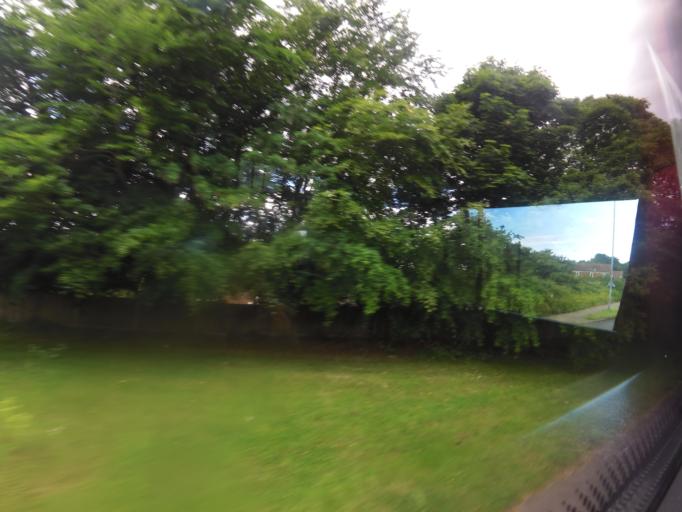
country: GB
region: England
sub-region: Norfolk
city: Cromer
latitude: 52.9186
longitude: 1.3069
